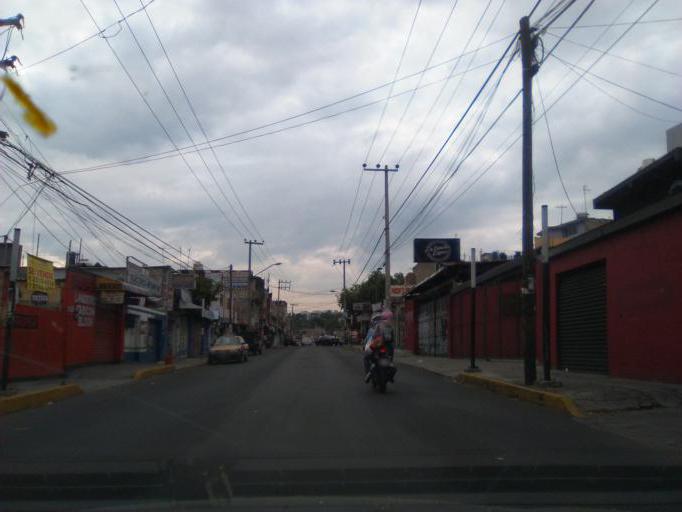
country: MX
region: Mexico City
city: Alvaro Obregon
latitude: 19.3671
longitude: -99.2347
